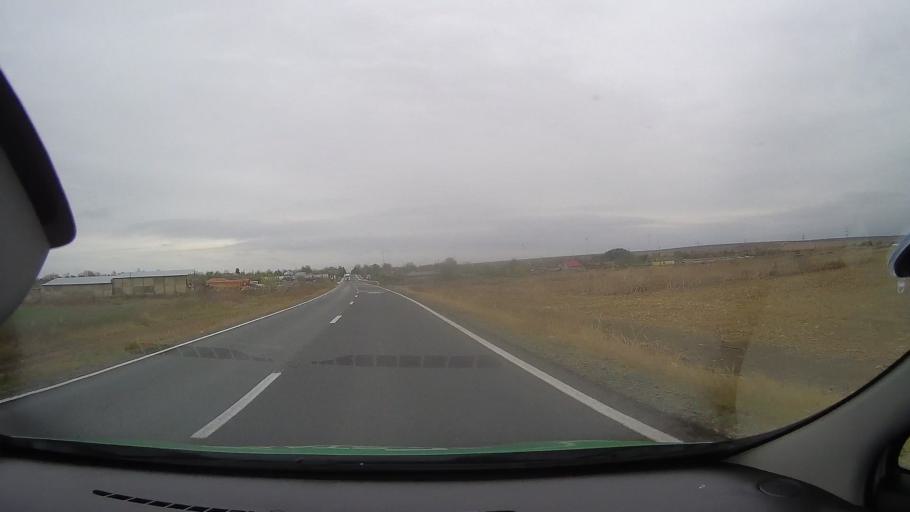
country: RO
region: Constanta
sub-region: Comuna Nicolae Balcescu
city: Dorobantu
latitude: 44.4136
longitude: 28.3189
